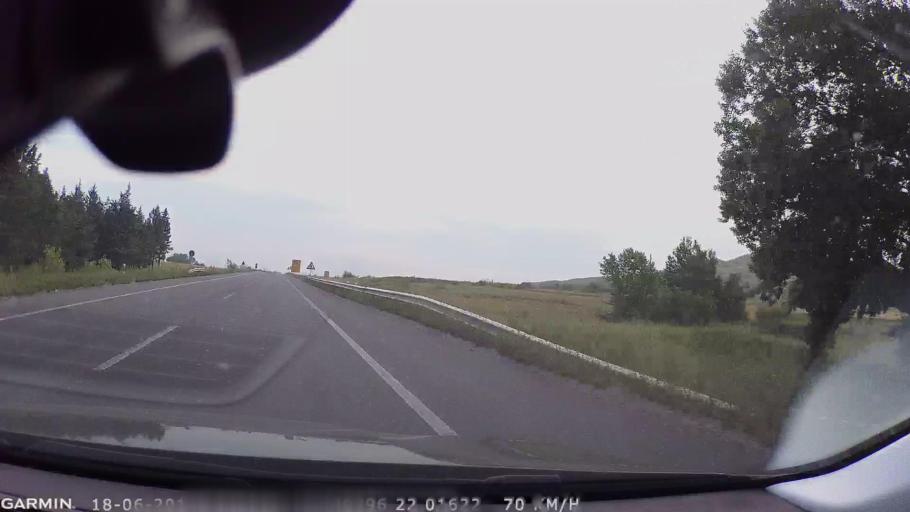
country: MK
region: Sveti Nikole
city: Sveti Nikole
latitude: 41.8026
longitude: 22.0151
